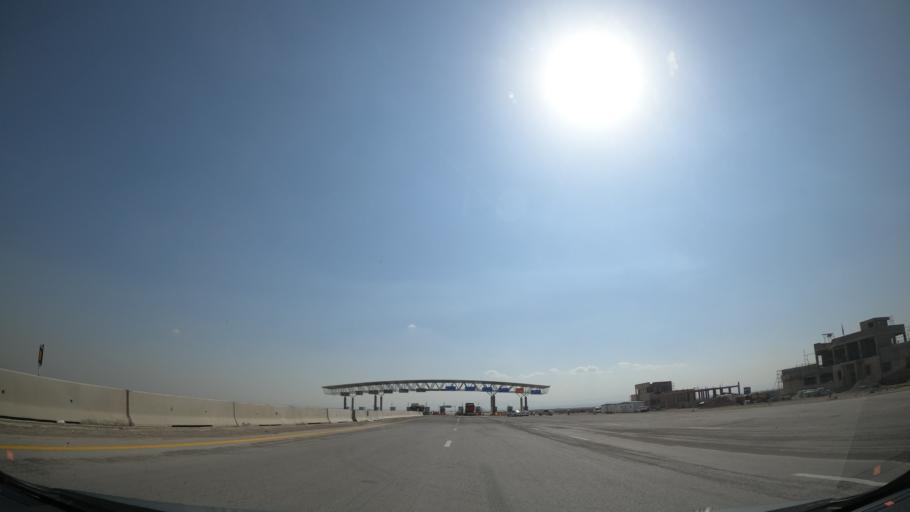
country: IR
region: Qazvin
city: Abyek
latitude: 35.9595
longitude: 50.4642
